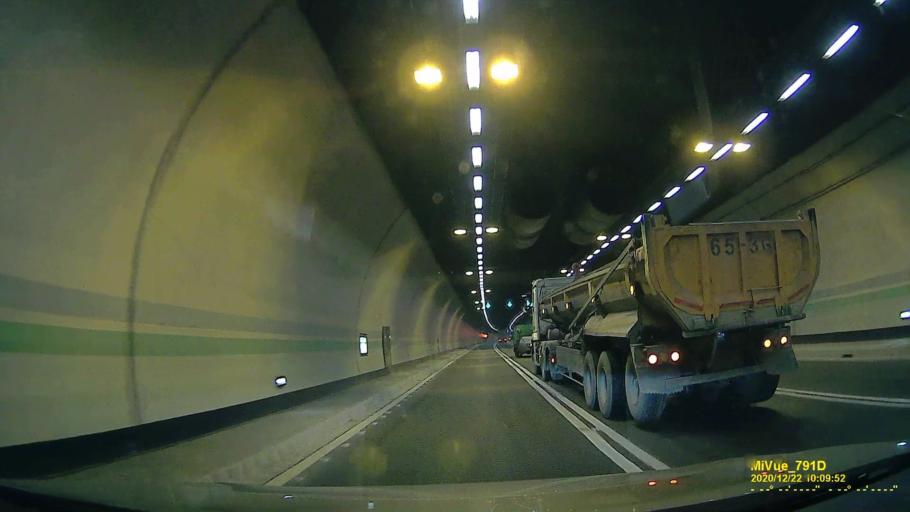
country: TW
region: Taiwan
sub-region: Pingtung
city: Pingtung
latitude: 22.8192
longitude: 120.4215
